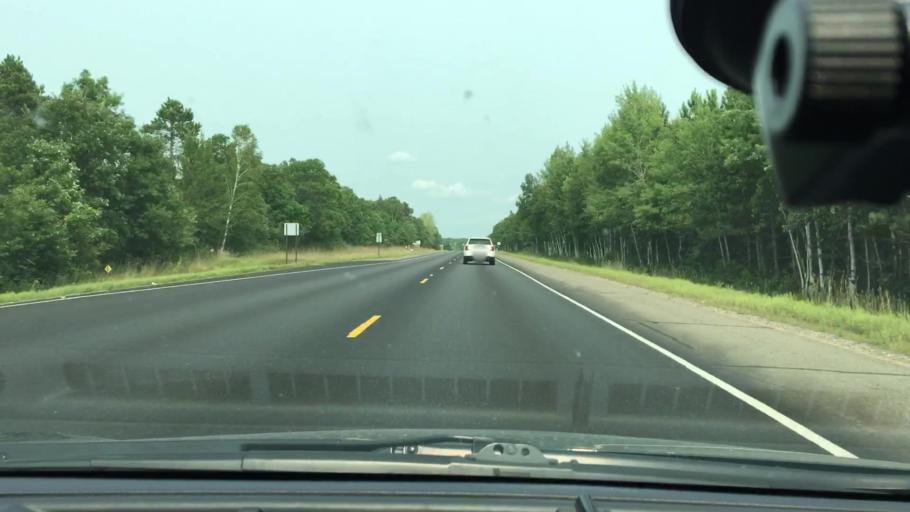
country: US
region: Minnesota
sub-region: Crow Wing County
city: Cross Lake
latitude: 46.6317
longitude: -94.1252
